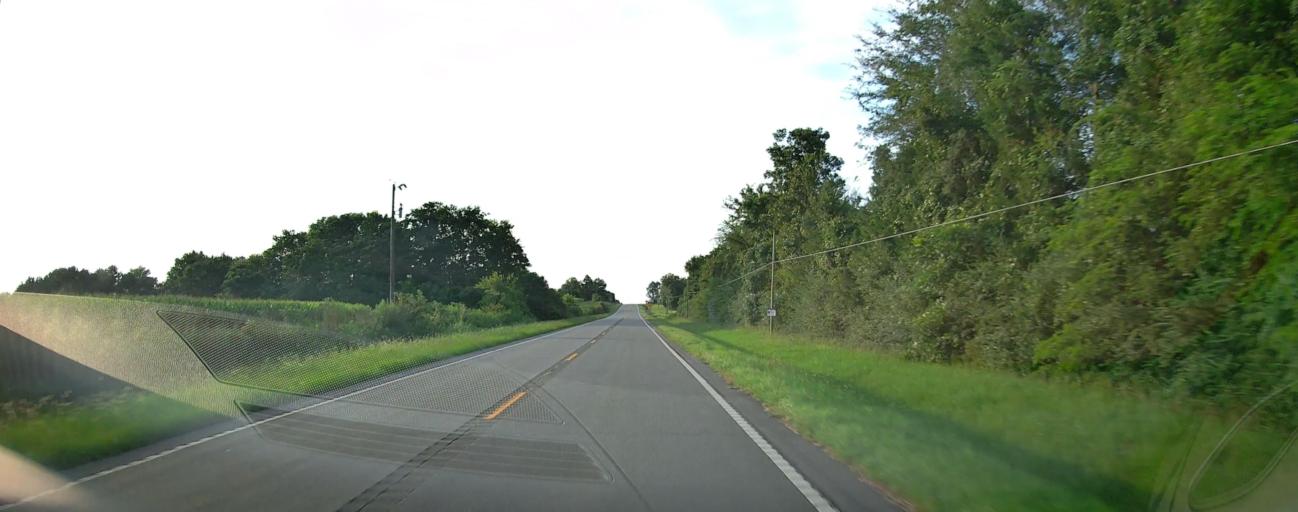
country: US
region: Georgia
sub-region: Taylor County
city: Reynolds
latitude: 32.5916
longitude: -84.0910
